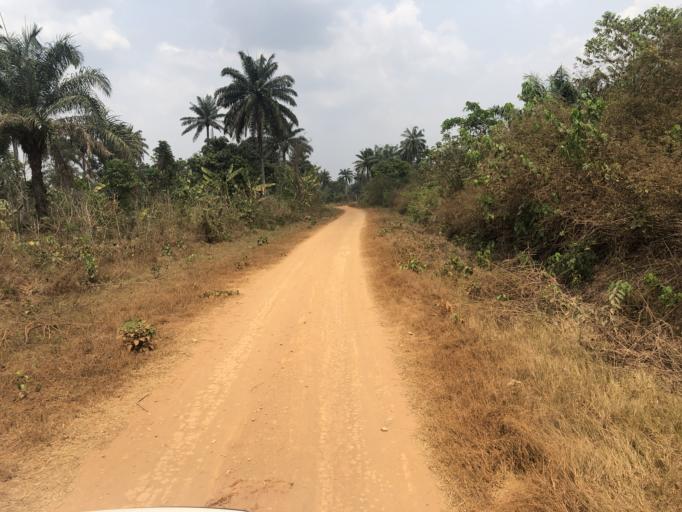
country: NG
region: Osun
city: Bode Osi
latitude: 7.7569
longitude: 4.2668
